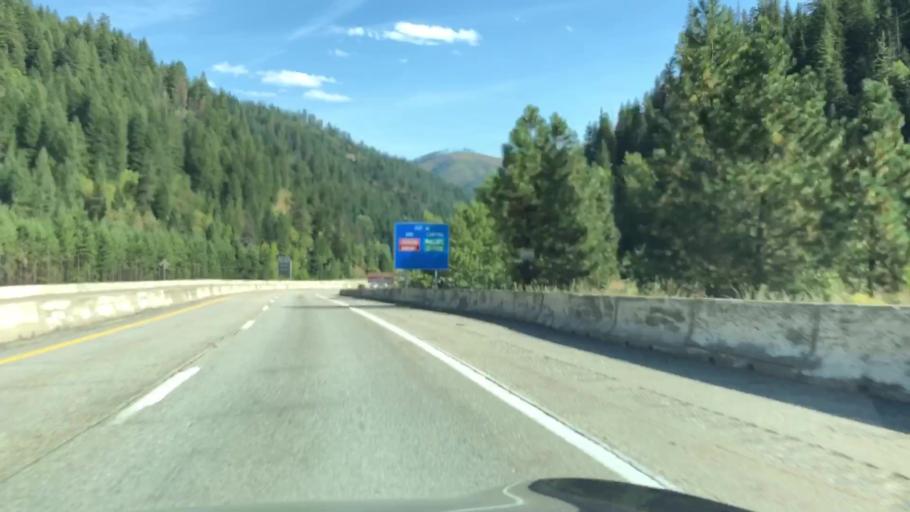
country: US
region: Idaho
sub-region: Shoshone County
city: Wallace
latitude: 47.4876
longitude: -115.9475
